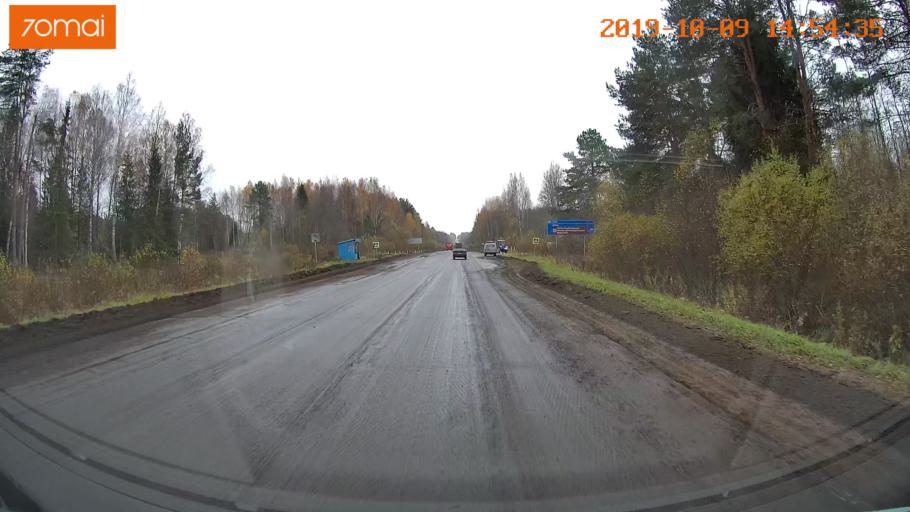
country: RU
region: Kostroma
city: Chistyye Bory
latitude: 58.3556
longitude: 41.6433
